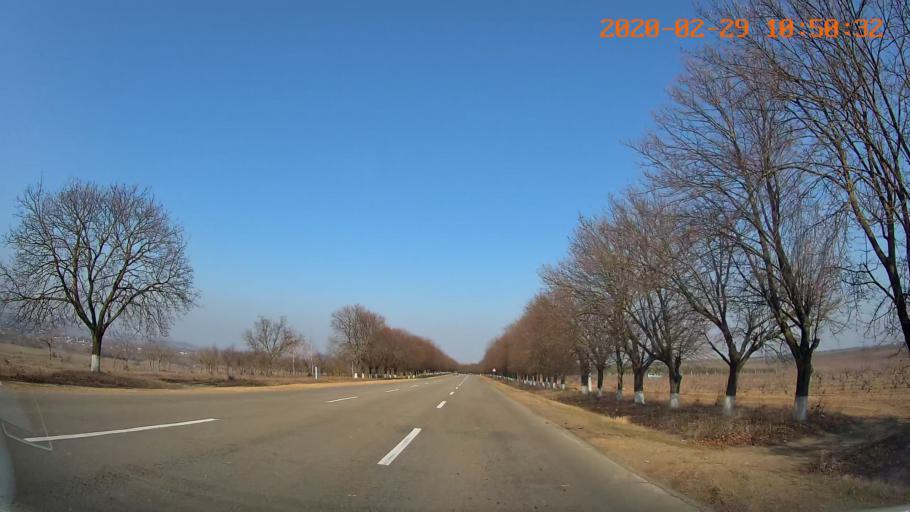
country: MD
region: Telenesti
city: Grigoriopol
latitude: 47.0842
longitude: 29.3742
